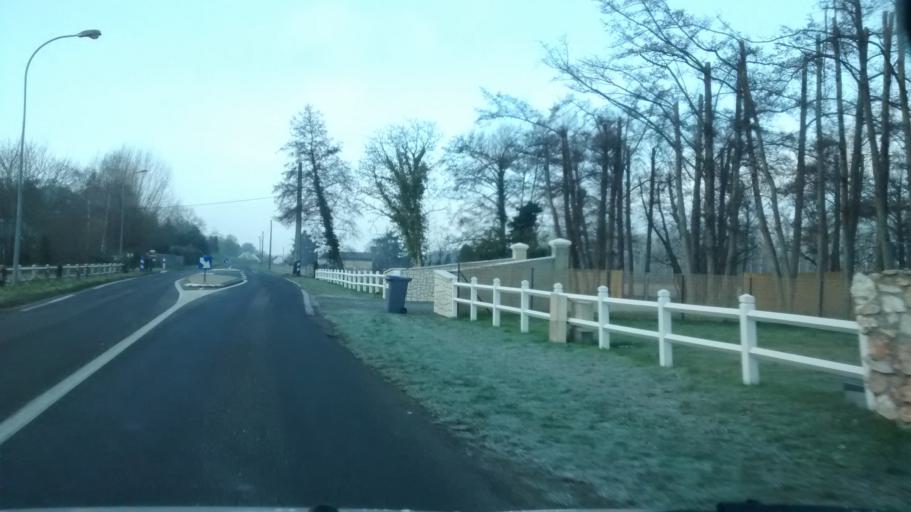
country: FR
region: Centre
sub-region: Departement d'Indre-et-Loire
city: Ballan-Mire
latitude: 47.3558
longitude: 0.5892
